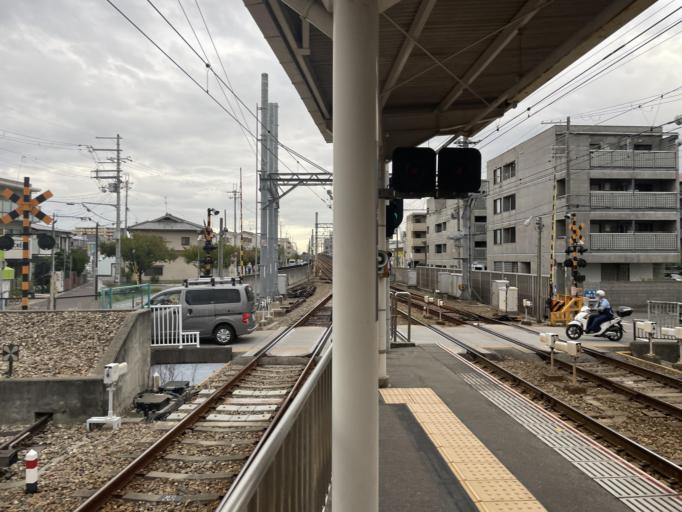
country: JP
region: Hyogo
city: Itami
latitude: 34.7530
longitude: 135.4173
